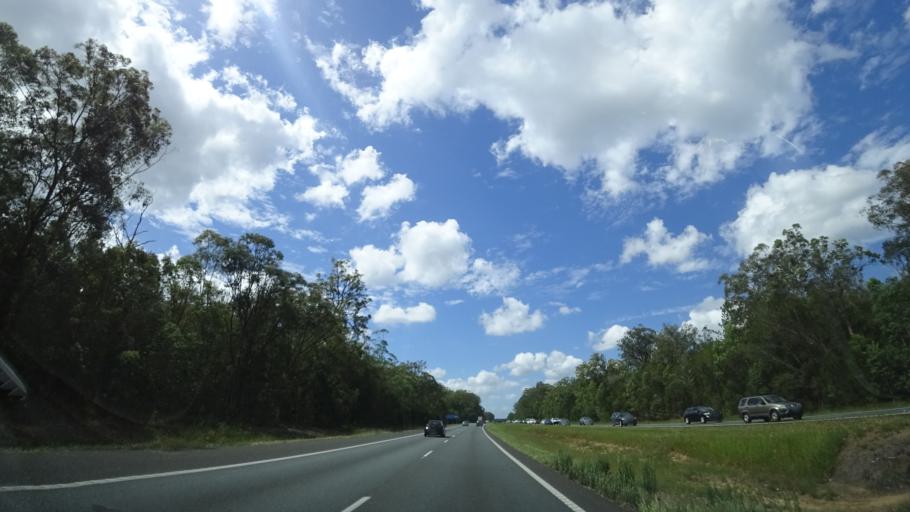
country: AU
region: Queensland
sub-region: Moreton Bay
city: Caboolture
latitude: -27.0145
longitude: 152.9769
